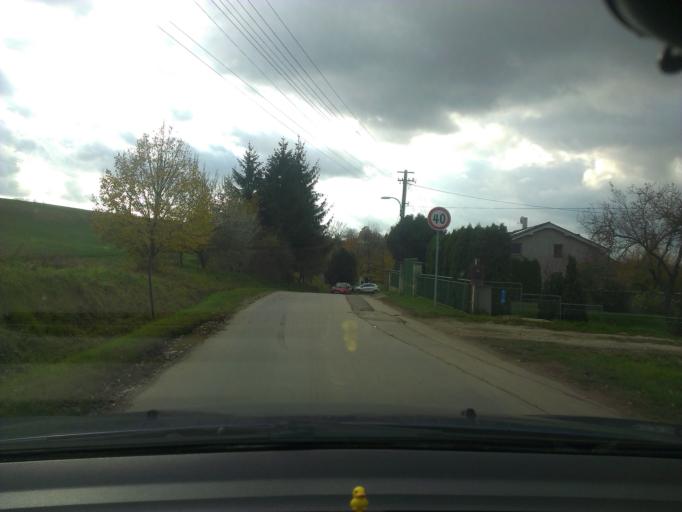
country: SK
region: Trnavsky
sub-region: Okres Trnava
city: Piestany
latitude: 48.6031
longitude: 17.8704
